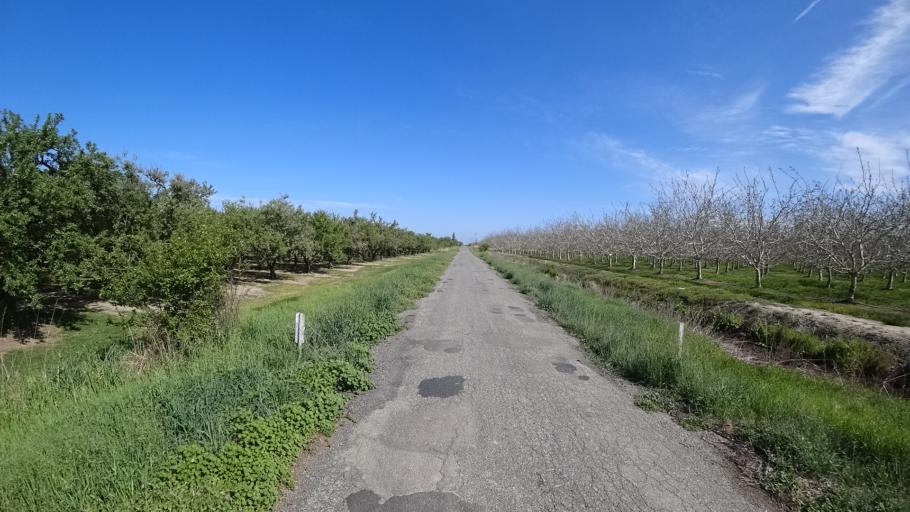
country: US
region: California
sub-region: Glenn County
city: Hamilton City
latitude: 39.6278
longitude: -122.0181
